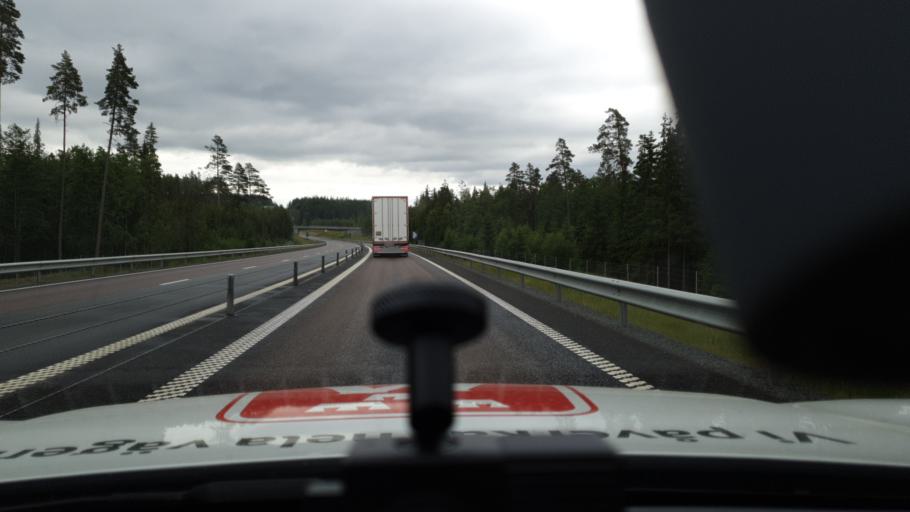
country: SE
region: Joenkoeping
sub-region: Mullsjo Kommun
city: Mullsjoe
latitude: 57.8901
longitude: 13.8898
